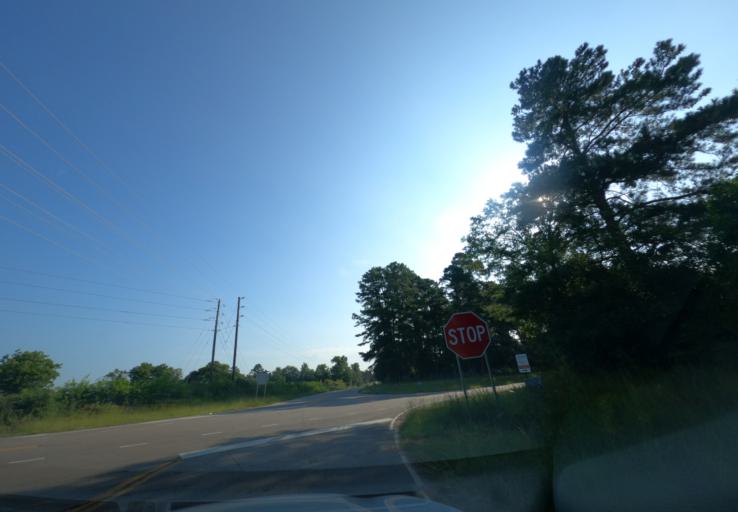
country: US
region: South Carolina
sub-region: Edgefield County
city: Murphys Estates
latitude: 33.6009
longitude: -81.9761
